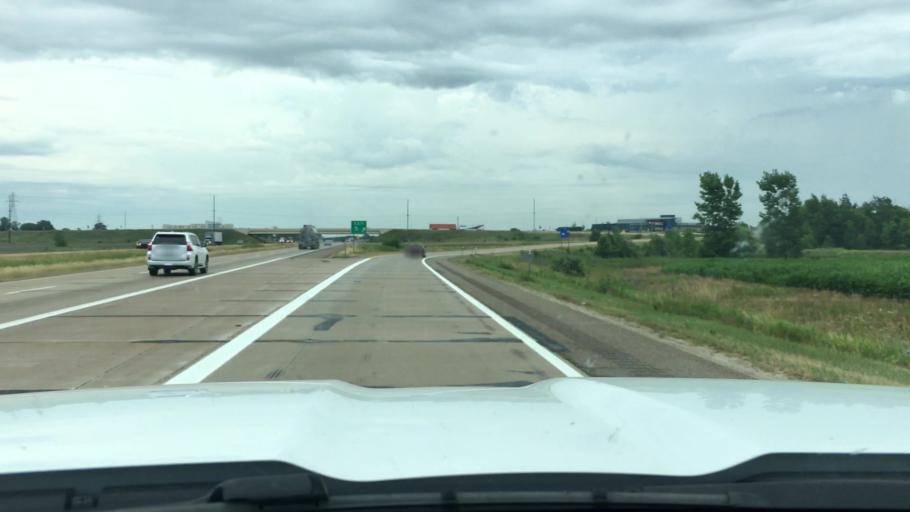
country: US
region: Michigan
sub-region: Kent County
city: Byron Center
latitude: 42.8526
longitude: -85.7299
